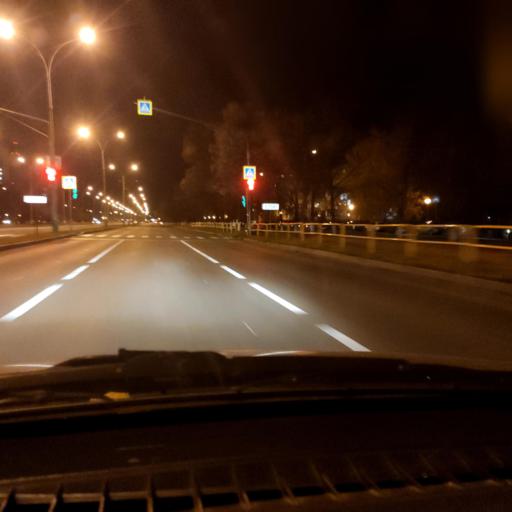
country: RU
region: Samara
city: Tol'yatti
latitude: 53.5298
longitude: 49.2729
